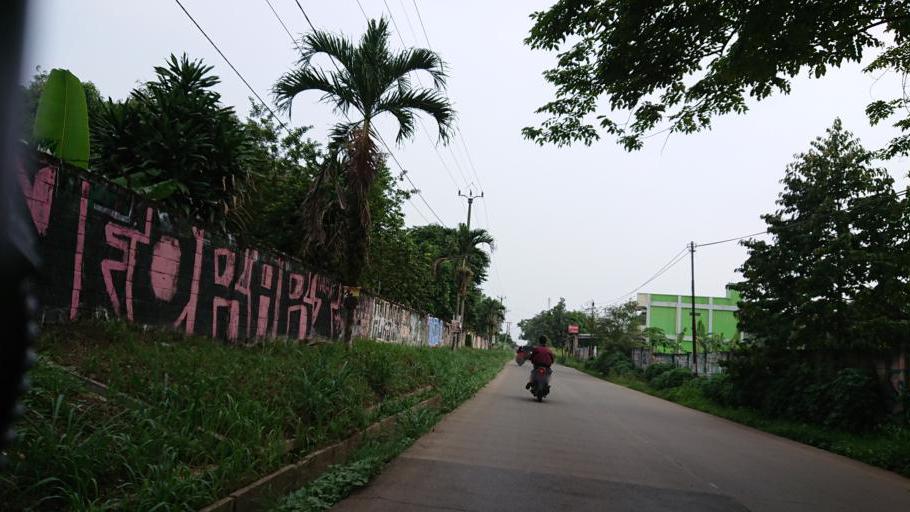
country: ID
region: West Java
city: Parung
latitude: -6.4008
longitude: 106.6898
